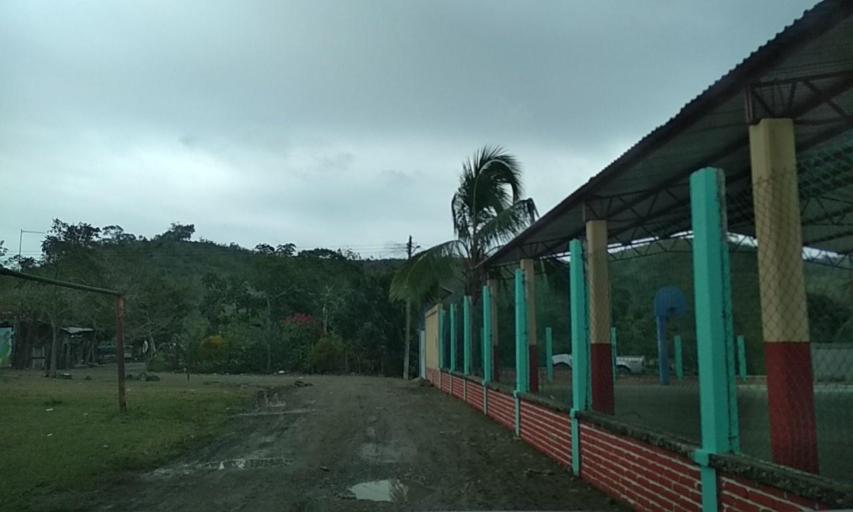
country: MX
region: Veracruz
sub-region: Coatzintla
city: Manuel Maria Contreras
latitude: 20.3585
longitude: -97.5115
